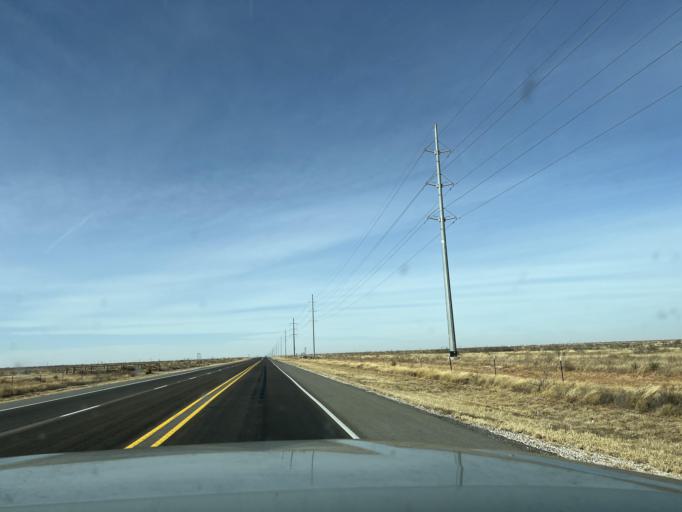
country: US
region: Texas
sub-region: Andrews County
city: Andrews
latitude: 32.3407
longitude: -102.6895
